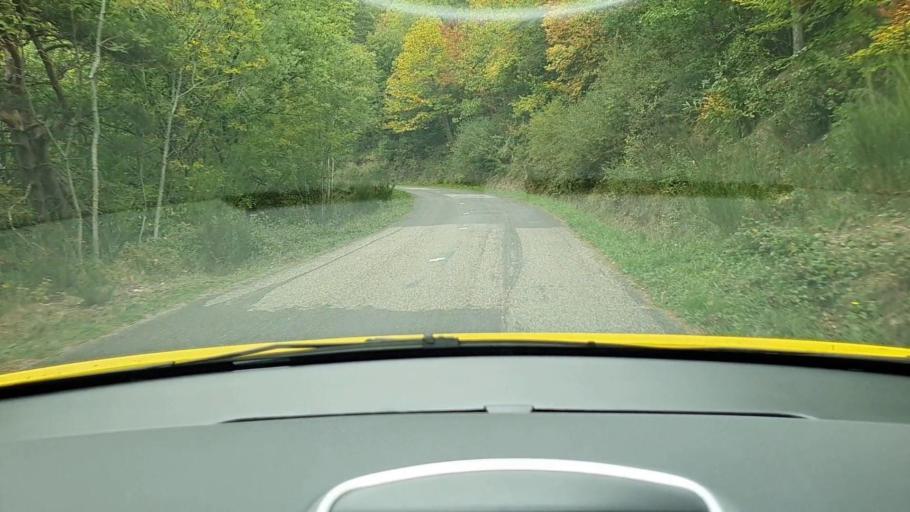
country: FR
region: Languedoc-Roussillon
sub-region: Departement de la Lozere
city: Meyrueis
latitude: 44.0780
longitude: 3.4150
